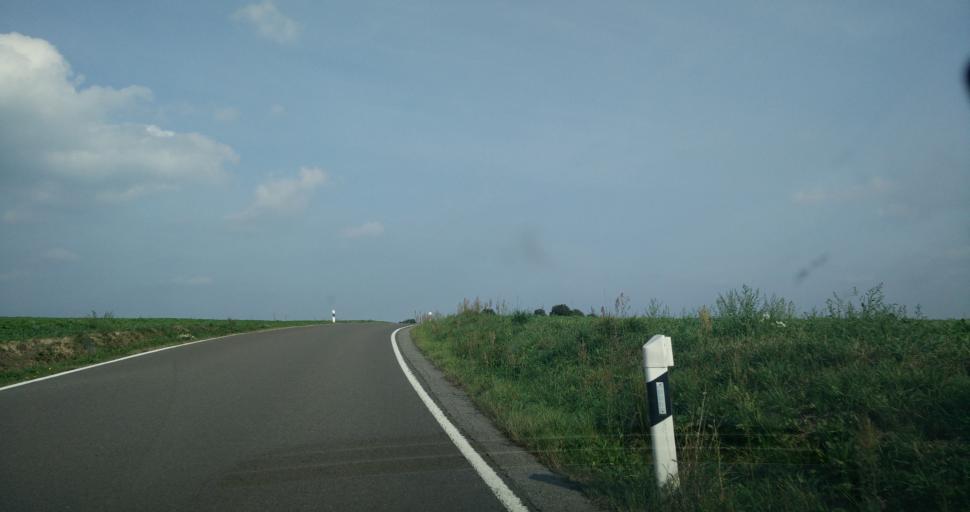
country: DE
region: Saxony
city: Colditz
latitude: 51.0904
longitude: 12.7953
